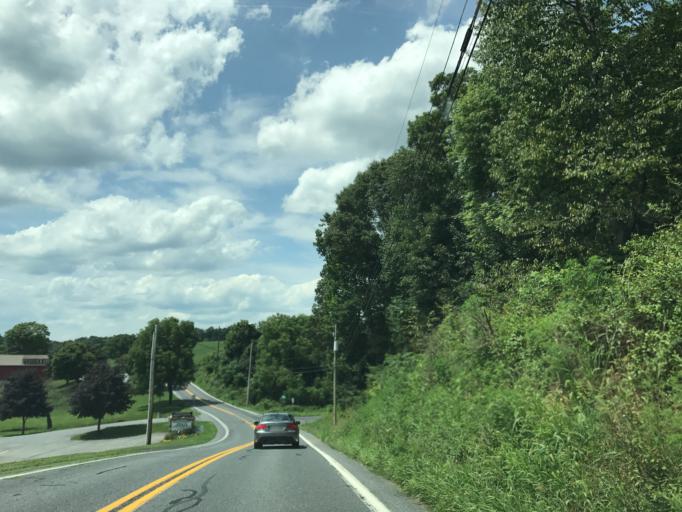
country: US
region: Pennsylvania
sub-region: Lancaster County
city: Brickerville
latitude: 40.2087
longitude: -76.3061
